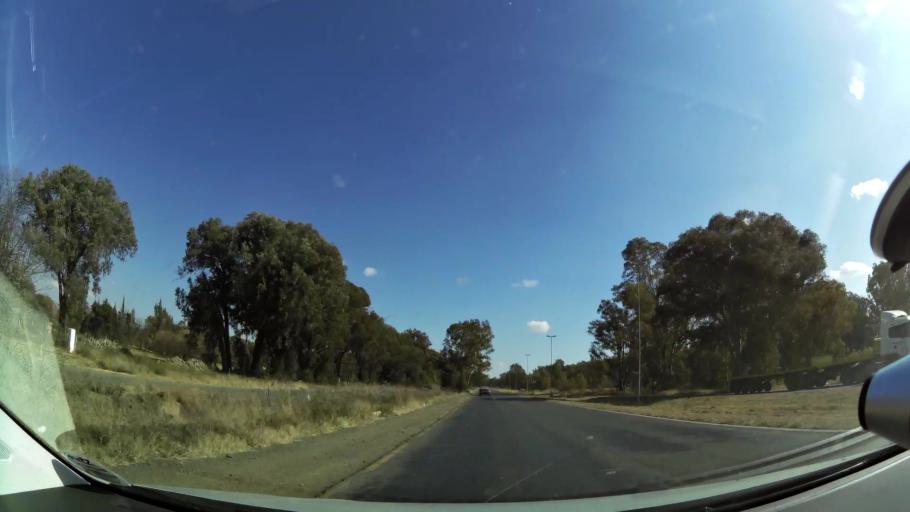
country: ZA
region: Orange Free State
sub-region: Mangaung Metropolitan Municipality
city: Bloemfontein
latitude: -29.1160
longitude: 26.2567
